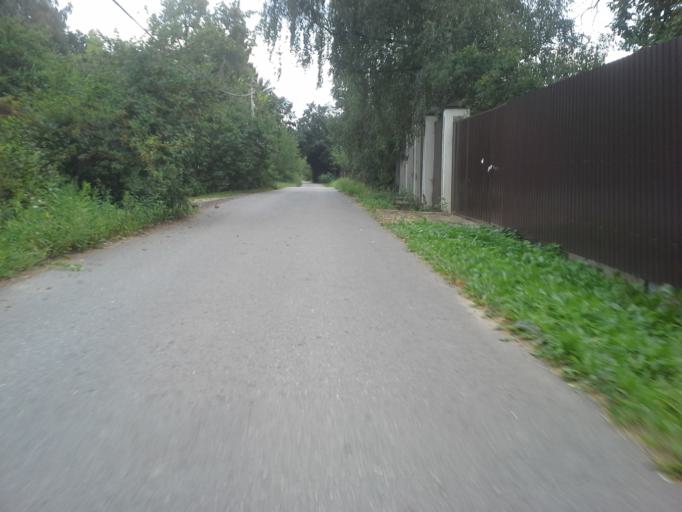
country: RU
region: Moskovskaya
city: Zhavoronki
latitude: 55.6351
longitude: 37.0678
